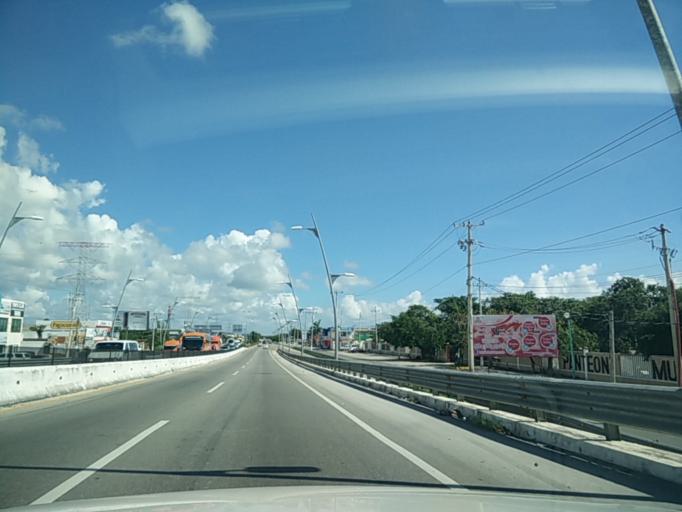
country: MX
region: Quintana Roo
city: Playa del Carmen
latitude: 20.6503
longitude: -87.0662
